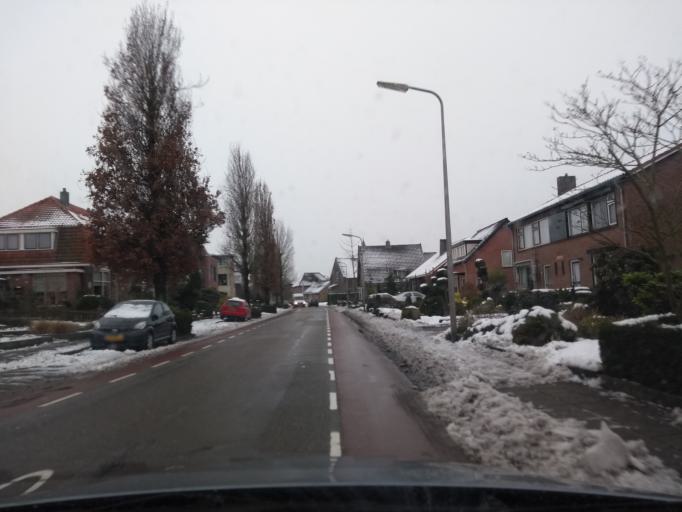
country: NL
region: Gelderland
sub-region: Gemeente Lochem
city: Barchem
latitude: 52.0904
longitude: 6.4500
